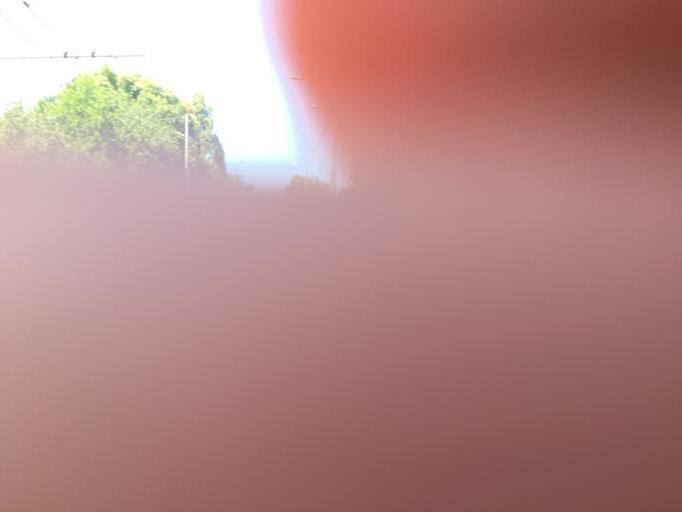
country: BG
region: Burgas
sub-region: Obshtina Burgas
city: Burgas
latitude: 42.4908
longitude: 27.4638
